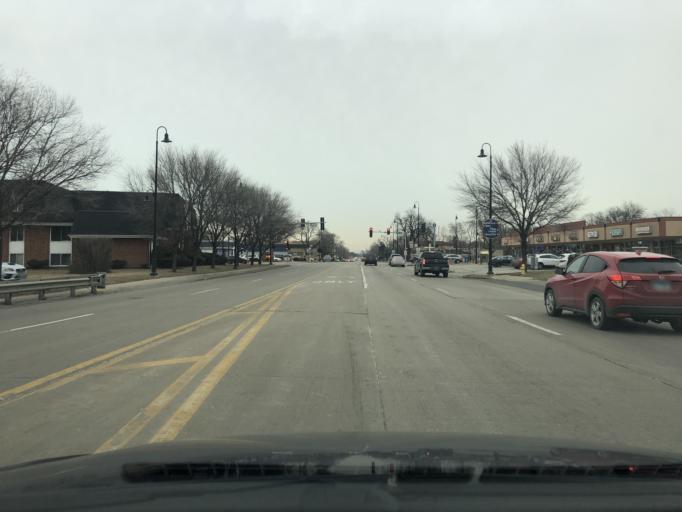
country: US
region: Illinois
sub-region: Cook County
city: Berkeley
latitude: 41.8896
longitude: -87.9147
